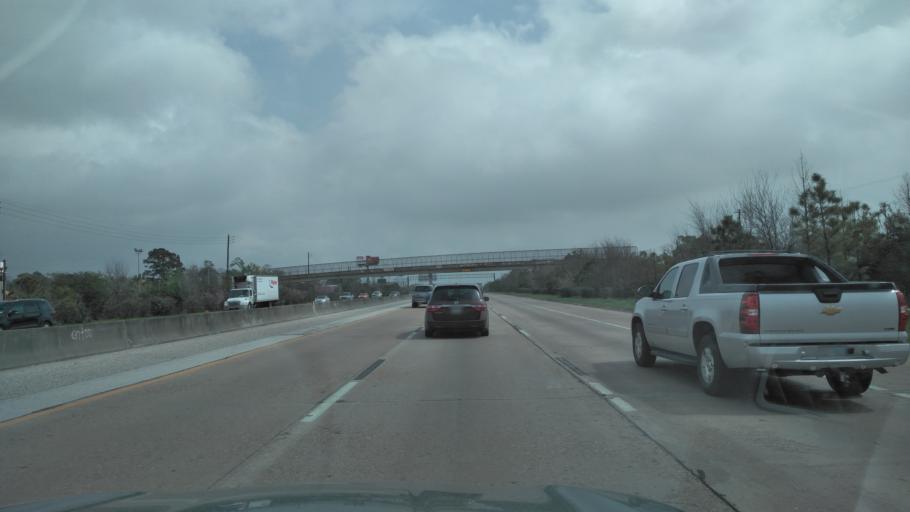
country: US
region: Texas
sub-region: Harris County
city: Channelview
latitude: 29.7803
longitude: -95.1179
